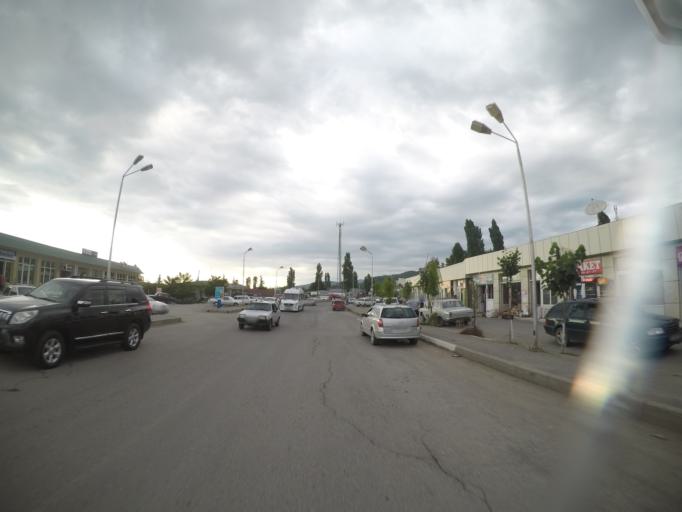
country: AZ
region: Qabala Rayon
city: Qutqashen
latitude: 40.9454
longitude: 47.9436
